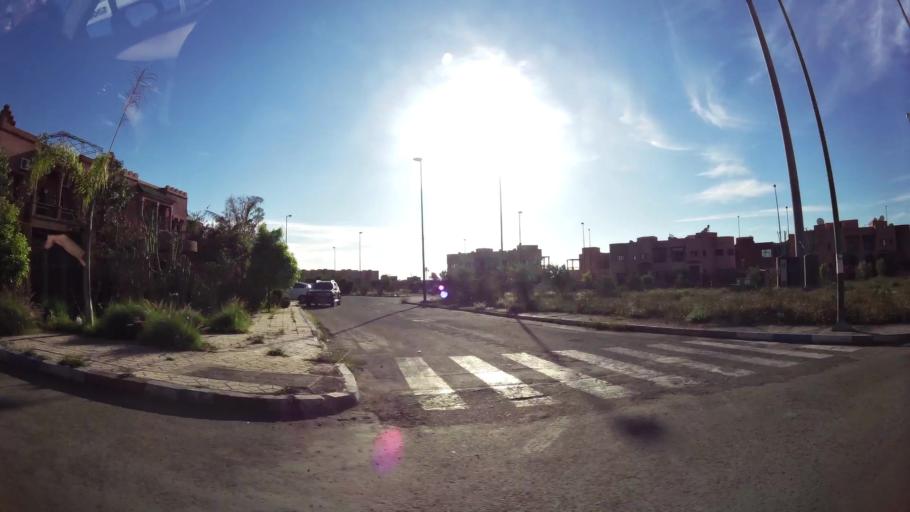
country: MA
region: Marrakech-Tensift-Al Haouz
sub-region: Marrakech
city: Marrakesh
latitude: 31.6746
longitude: -8.0590
